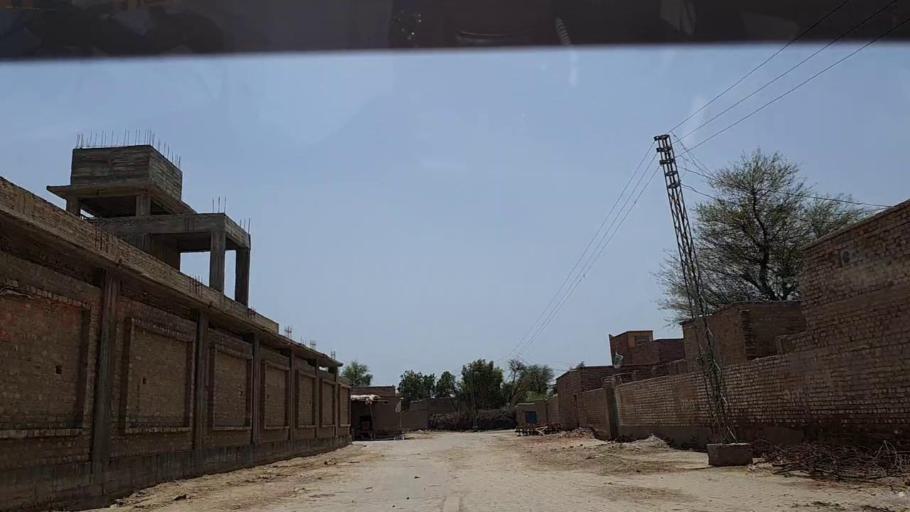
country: PK
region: Sindh
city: Dadu
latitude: 26.7126
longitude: 67.7350
